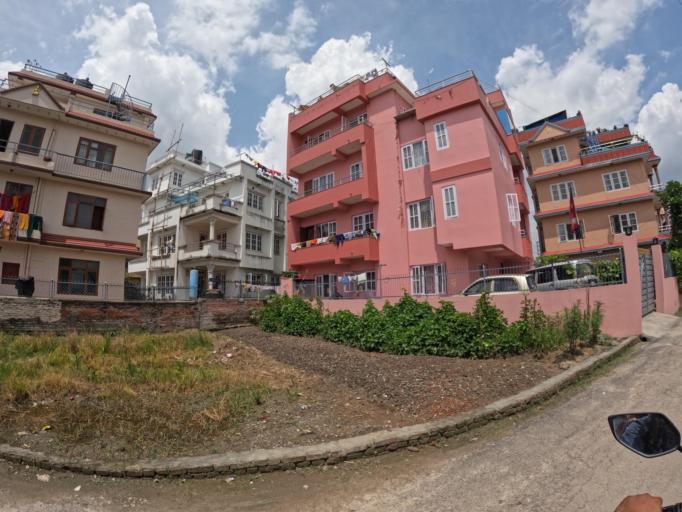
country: NP
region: Central Region
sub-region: Bagmati Zone
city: Kathmandu
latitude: 27.6781
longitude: 85.3705
